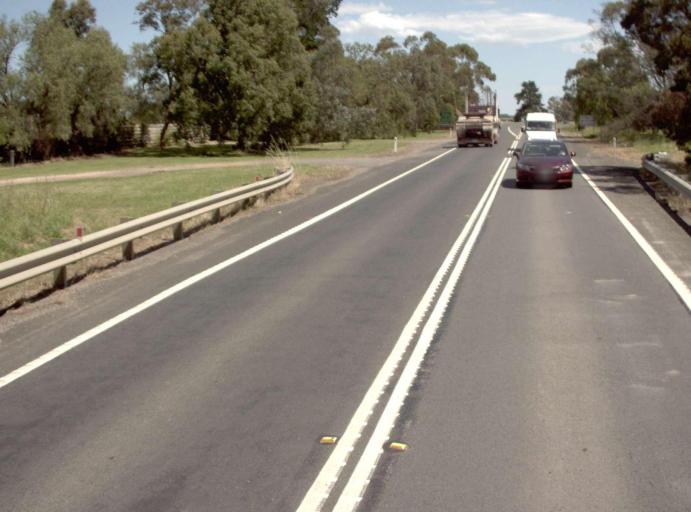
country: AU
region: Victoria
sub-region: Wellington
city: Sale
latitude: -37.9790
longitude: 147.0726
